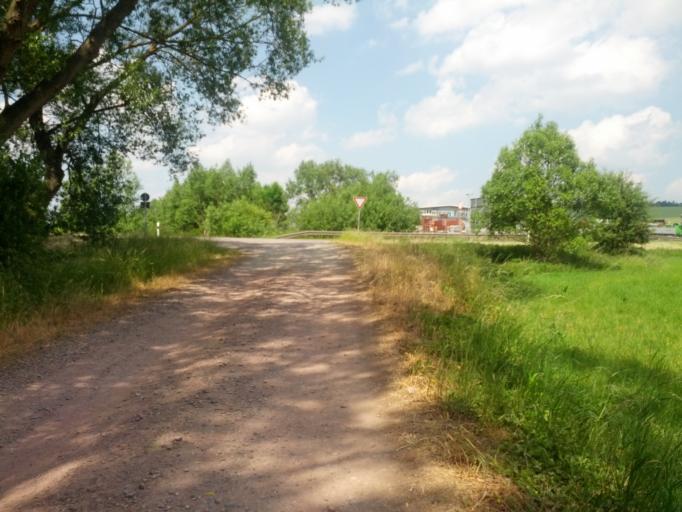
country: DE
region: Thuringia
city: Eisenach
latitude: 50.9994
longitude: 10.3214
